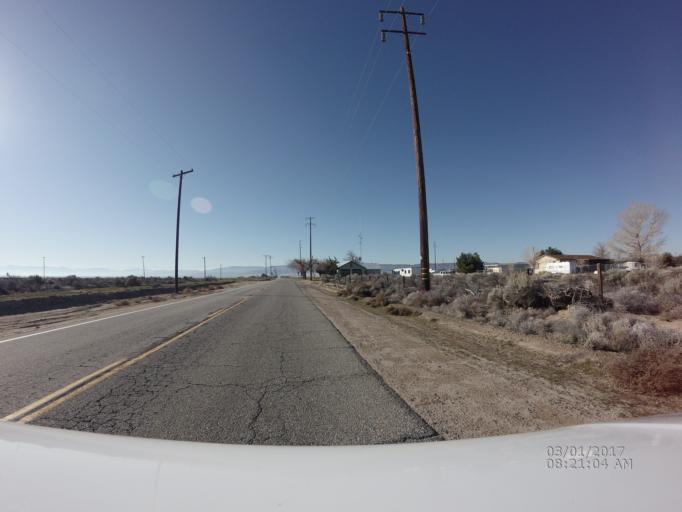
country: US
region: California
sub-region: Los Angeles County
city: Quartz Hill
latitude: 34.7342
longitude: -118.2549
